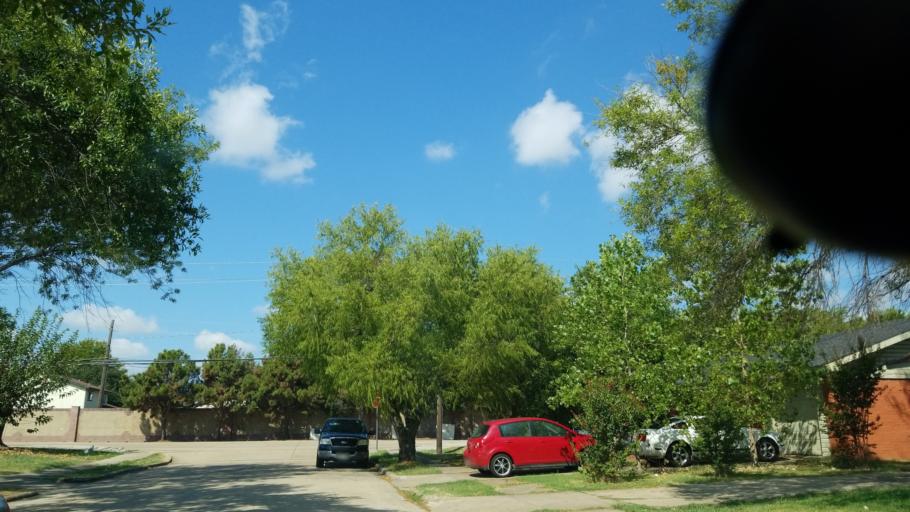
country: US
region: Texas
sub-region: Dallas County
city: Grand Prairie
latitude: 32.7056
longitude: -96.9936
